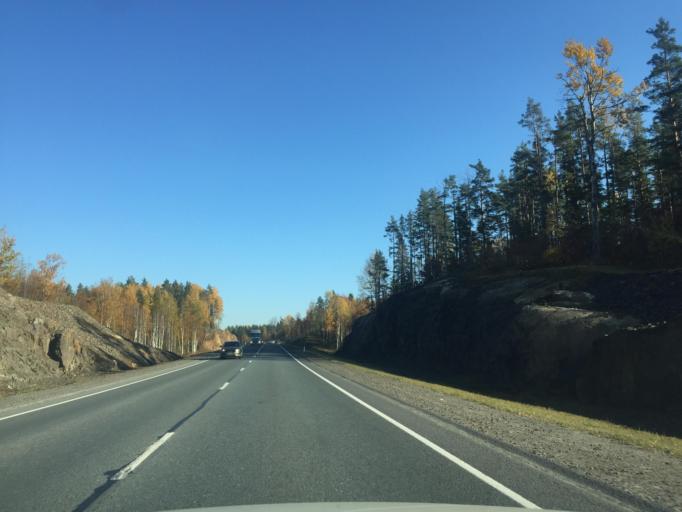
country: RU
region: Leningrad
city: Kuznechnoye
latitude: 61.2927
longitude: 29.7737
